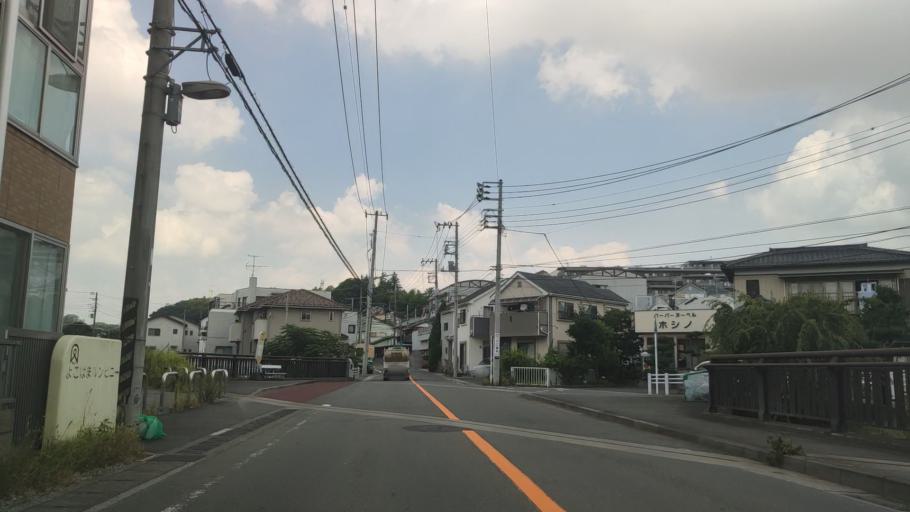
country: JP
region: Kanagawa
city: Minami-rinkan
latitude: 35.4358
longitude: 139.5134
